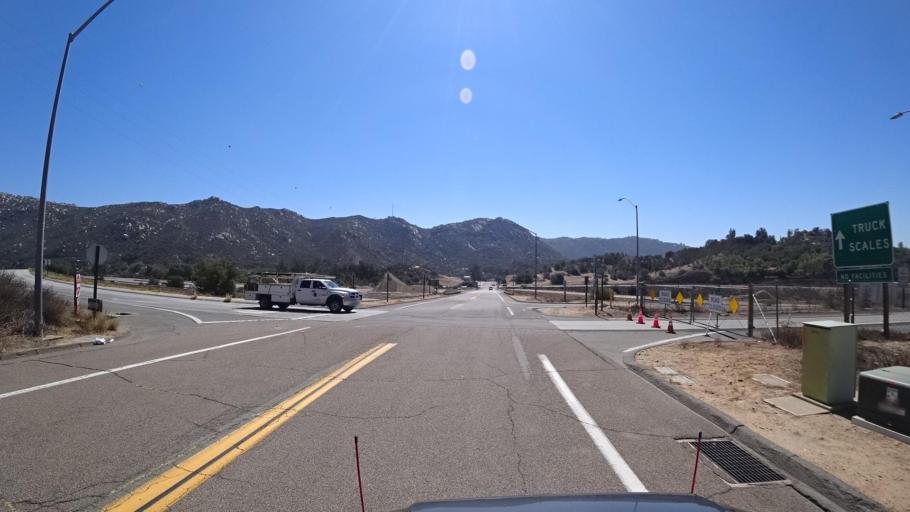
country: US
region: California
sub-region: San Diego County
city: Rainbow
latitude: 33.4314
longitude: -117.1469
